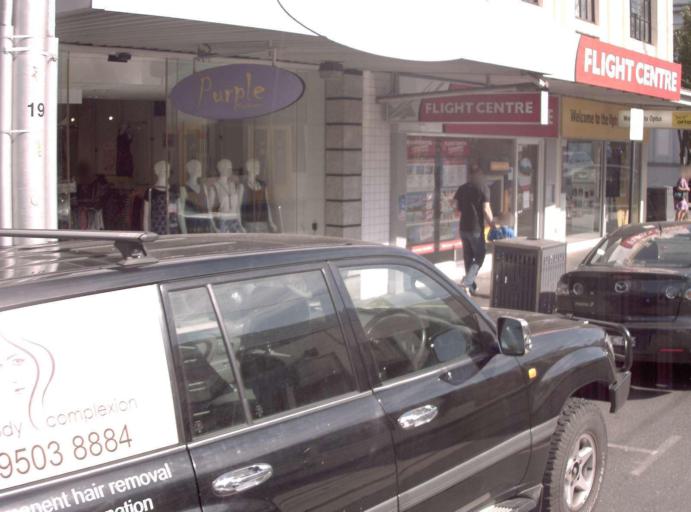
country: AU
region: Victoria
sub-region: Glen Eira
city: Caulfield North
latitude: -37.8617
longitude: 145.0284
